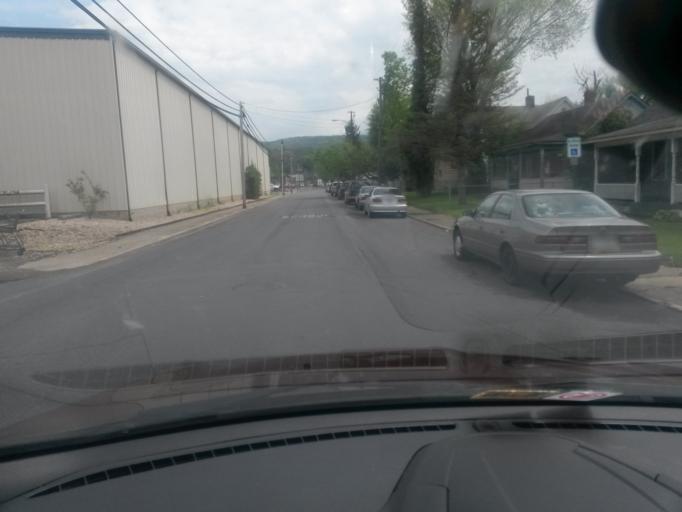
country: US
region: Virginia
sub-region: City of Covington
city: Covington
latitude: 37.7860
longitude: -79.9932
